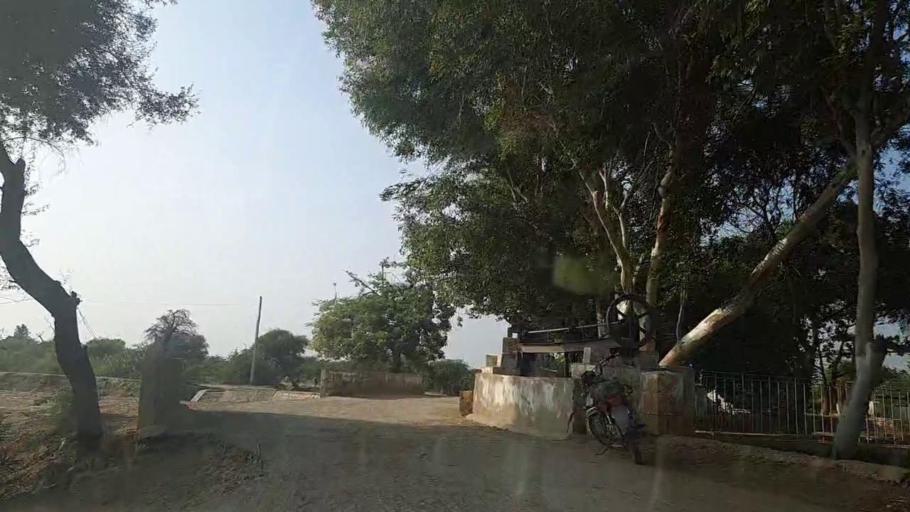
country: PK
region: Sindh
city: Mirpur Sakro
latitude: 24.5741
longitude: 67.6653
